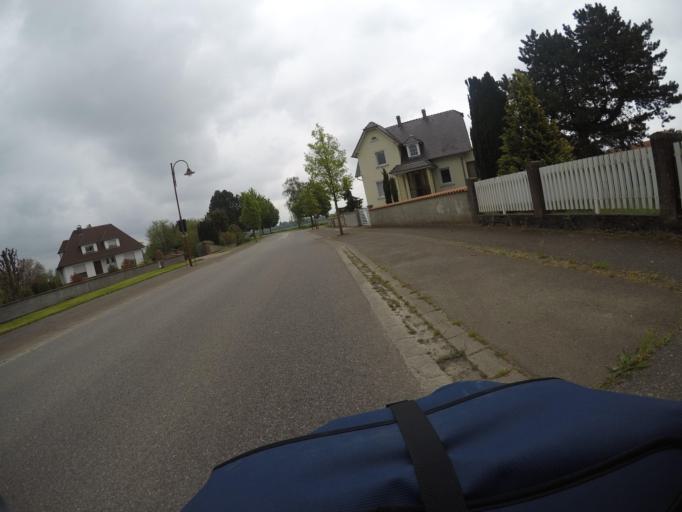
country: FR
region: Alsace
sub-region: Departement du Bas-Rhin
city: Drusenheim
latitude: 48.7666
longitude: 7.9573
